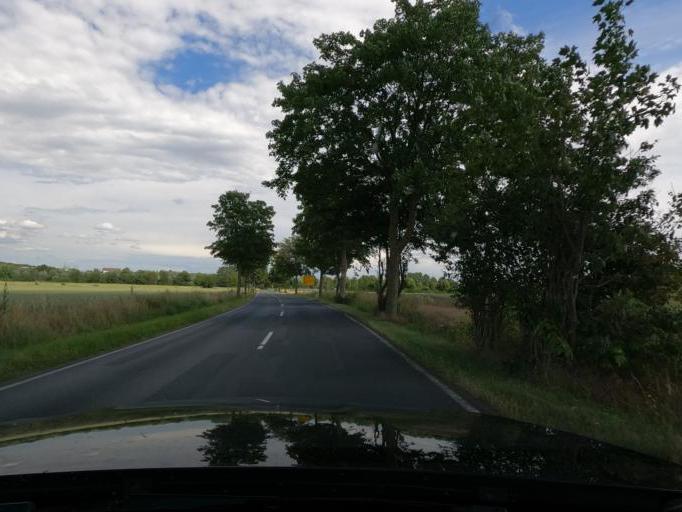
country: DE
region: Lower Saxony
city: Lengede
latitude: 52.1898
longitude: 10.3111
